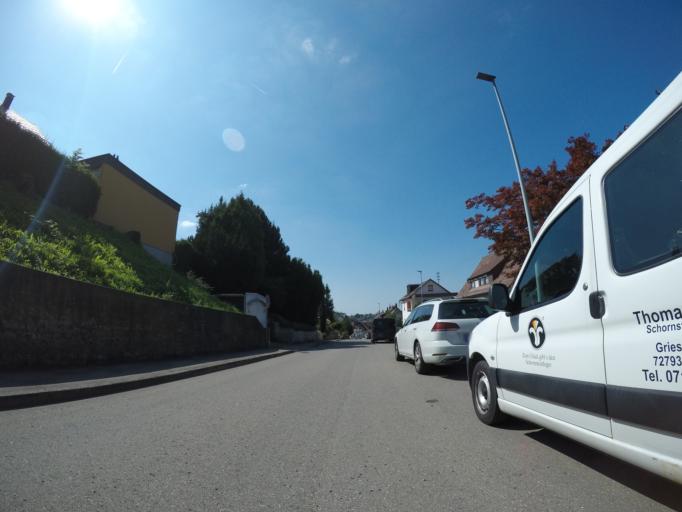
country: DE
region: Baden-Wuerttemberg
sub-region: Tuebingen Region
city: Eningen unter Achalm
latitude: 48.4828
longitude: 9.2629
